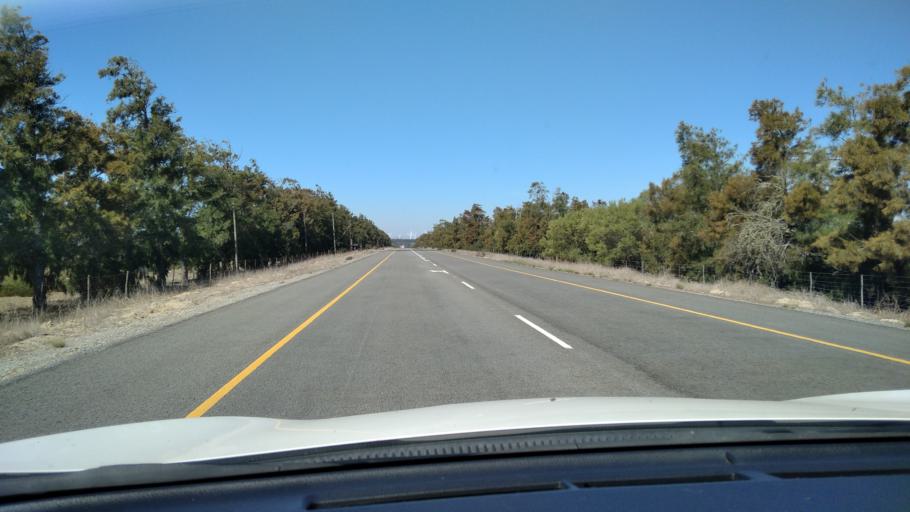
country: ZA
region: Western Cape
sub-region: West Coast District Municipality
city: Vredenburg
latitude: -33.0439
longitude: 18.3171
